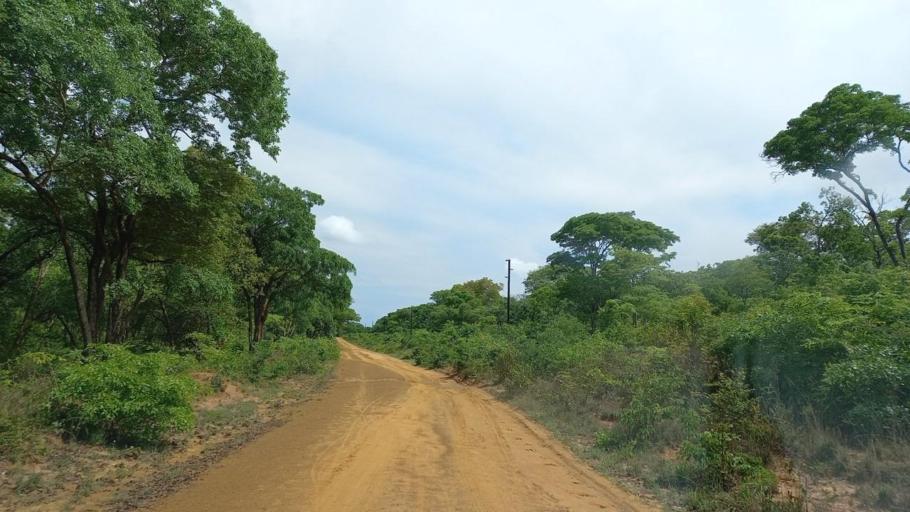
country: ZM
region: North-Western
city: Kabompo
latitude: -13.5346
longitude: 24.0958
